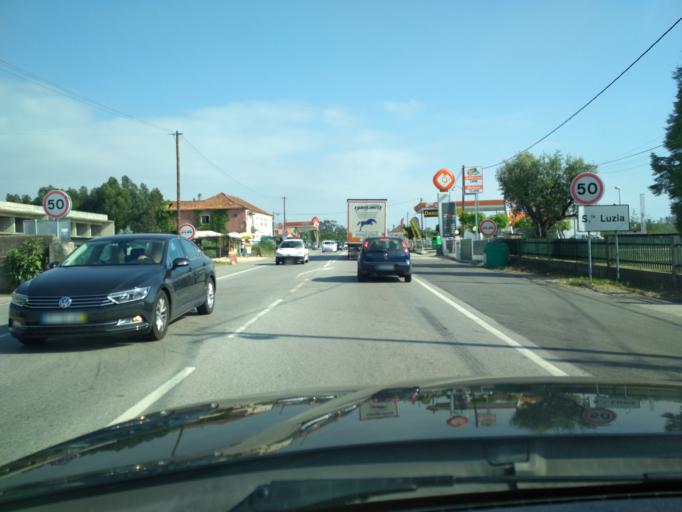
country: PT
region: Aveiro
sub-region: Mealhada
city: Pampilhosa do Botao
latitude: 40.3085
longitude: -8.4492
